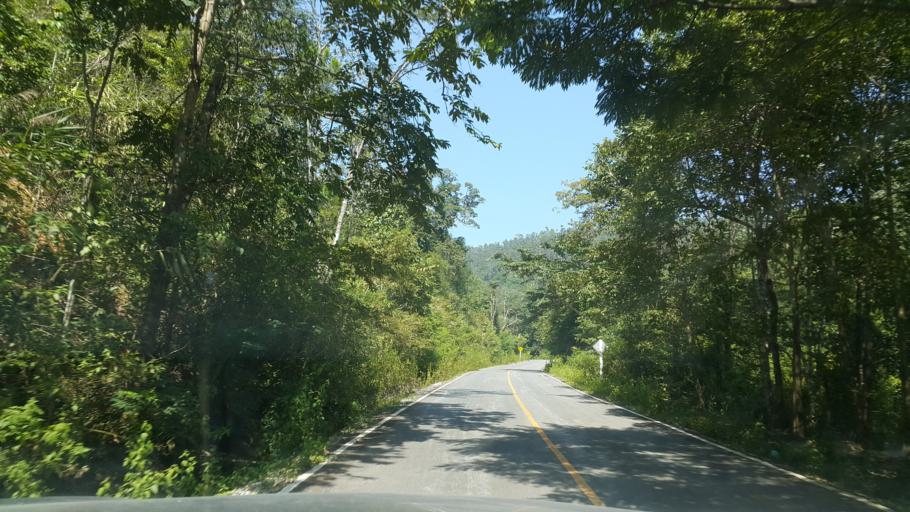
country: TH
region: Chiang Mai
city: Samoeng
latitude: 18.8962
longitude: 98.5999
